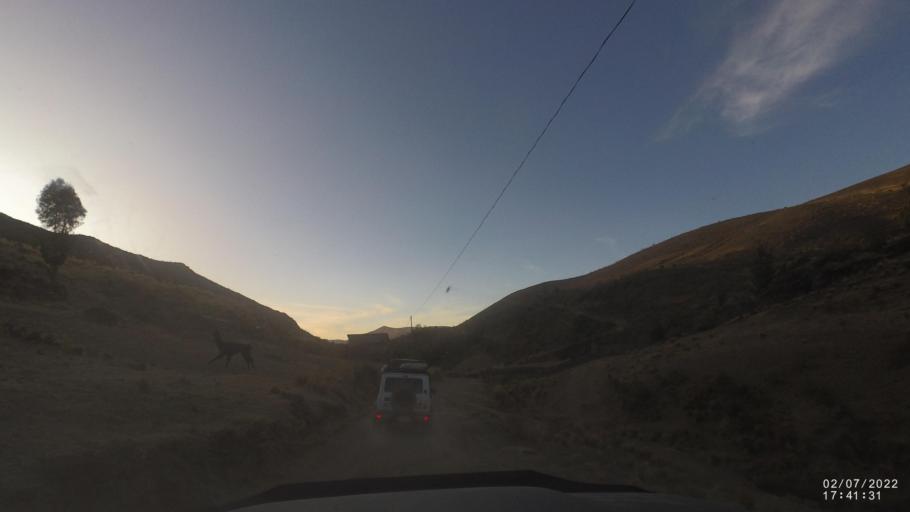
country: BO
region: Cochabamba
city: Irpa Irpa
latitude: -17.8611
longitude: -66.6140
